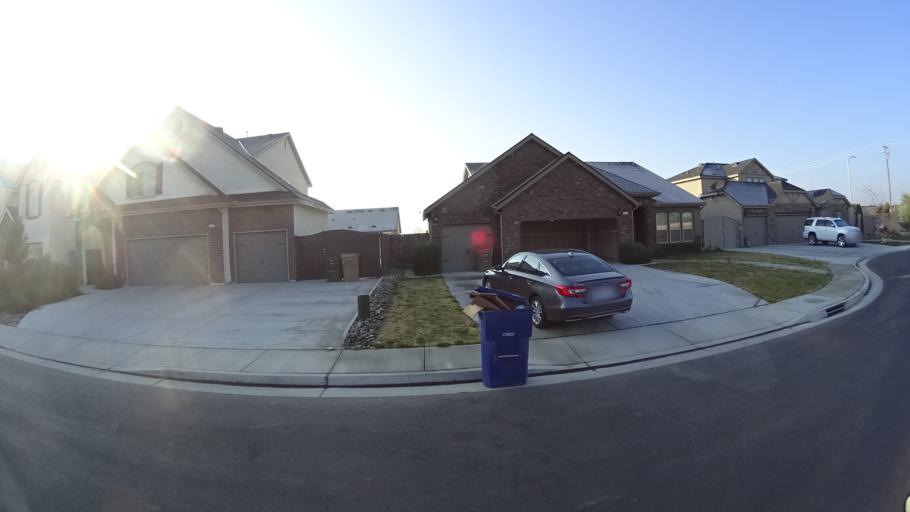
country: US
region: California
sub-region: Kern County
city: Greenacres
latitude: 35.2922
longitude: -119.1180
